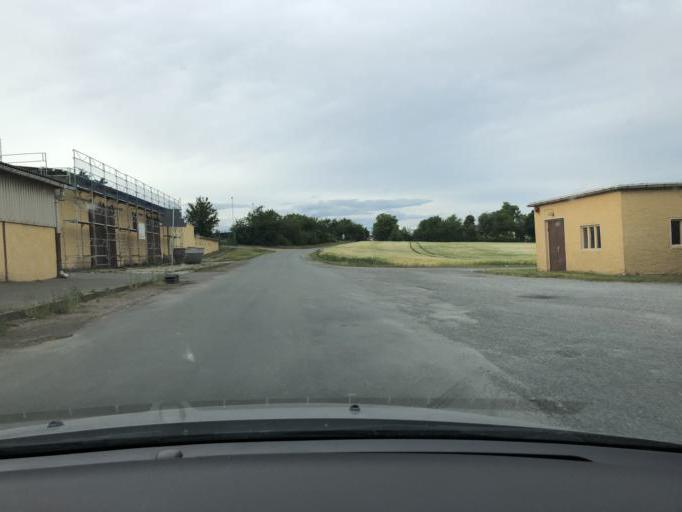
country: DE
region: Thuringia
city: Pfiffelbach
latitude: 51.0636
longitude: 11.4429
